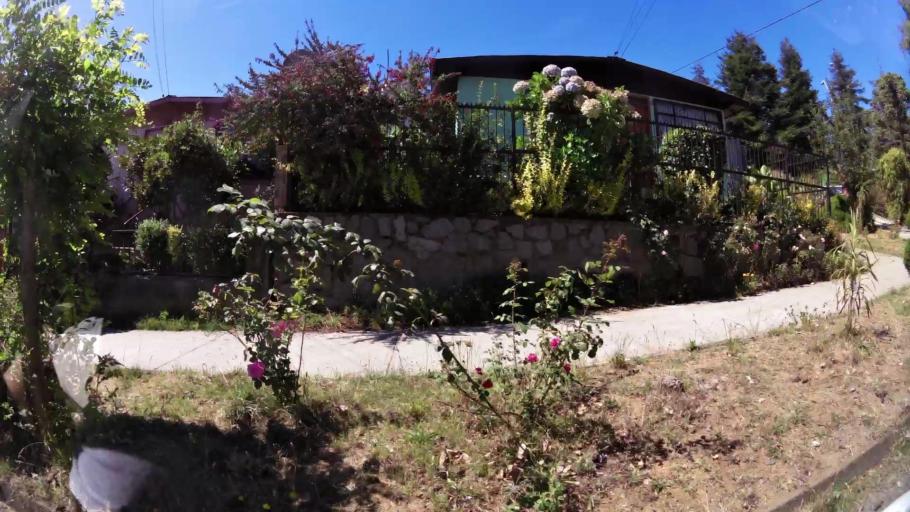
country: CL
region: Biobio
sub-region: Provincia de Concepcion
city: Penco
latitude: -36.7299
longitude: -72.9883
